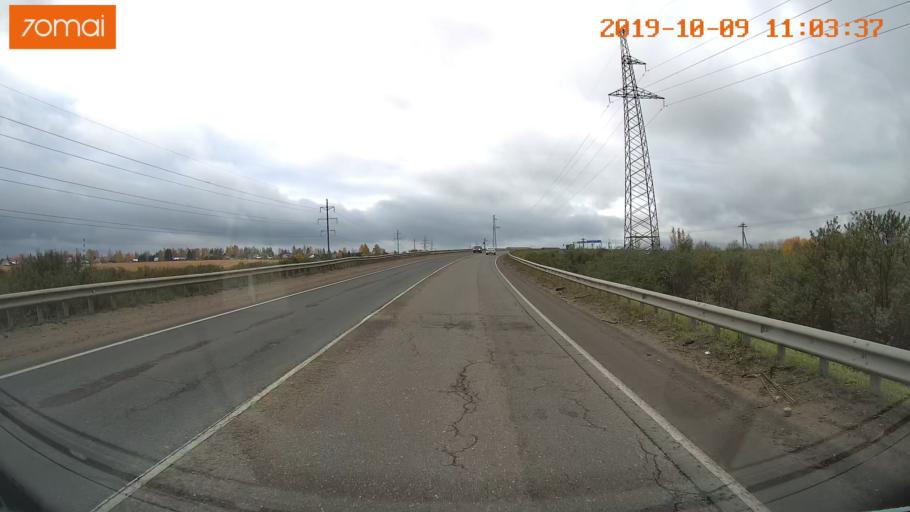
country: RU
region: Vologda
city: Vologda
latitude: 59.2190
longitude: 39.7739
